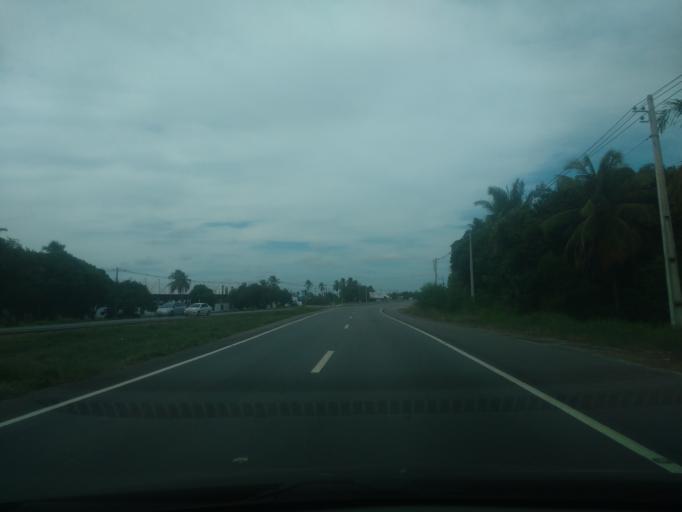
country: BR
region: Alagoas
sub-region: Maceio
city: Maceio
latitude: -9.7031
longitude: -35.8052
